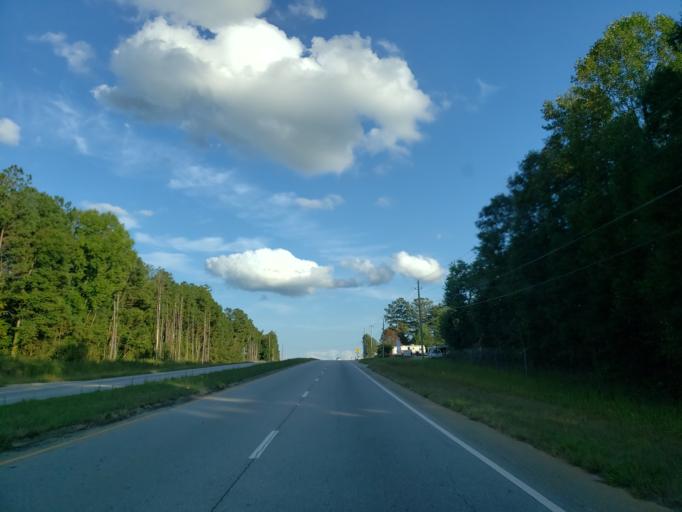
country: US
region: Georgia
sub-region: Carroll County
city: Carrollton
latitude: 33.6317
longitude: -85.1186
